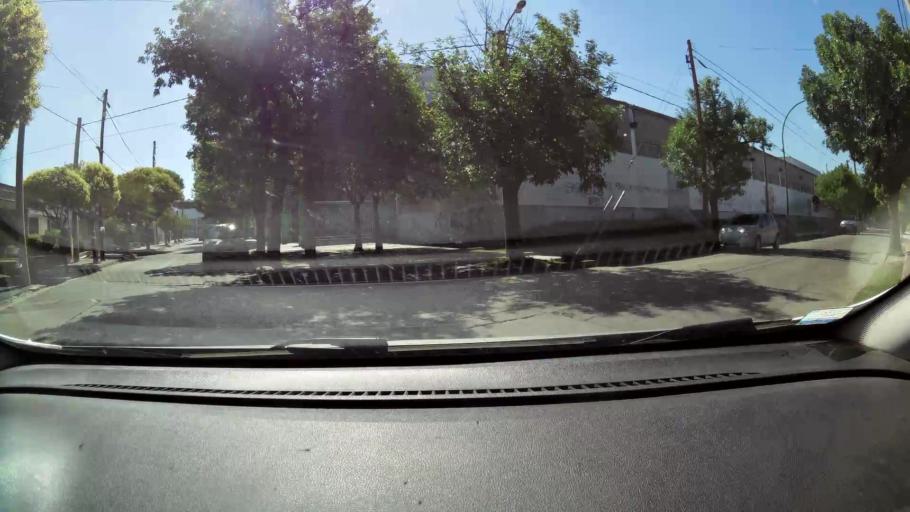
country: AR
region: Cordoba
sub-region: Departamento de Capital
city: Cordoba
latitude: -31.3798
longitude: -64.1749
